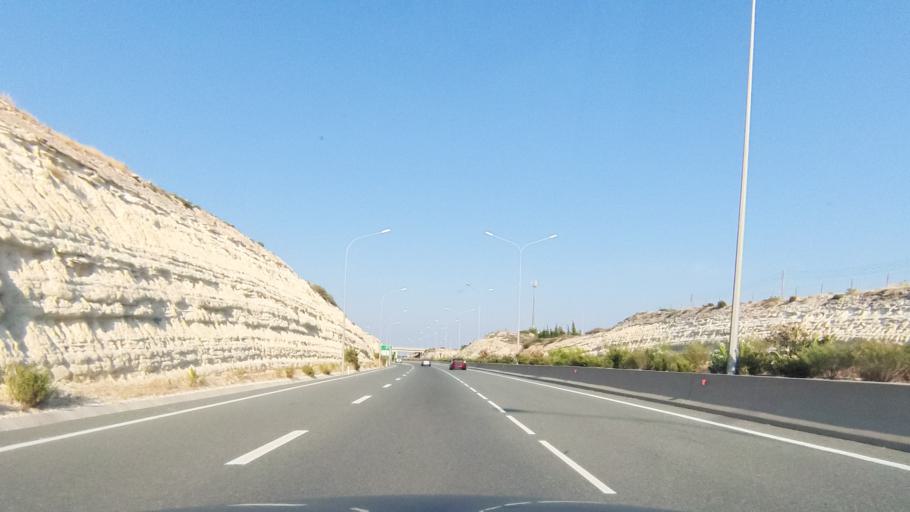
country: CY
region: Limassol
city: Erimi
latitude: 34.6822
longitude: 32.8838
